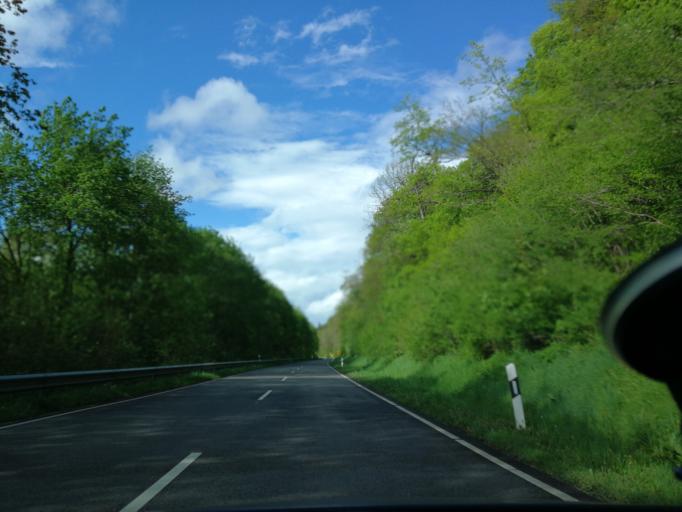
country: DE
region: Rheinland-Pfalz
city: Oberbillig
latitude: 49.7378
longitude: 6.5029
